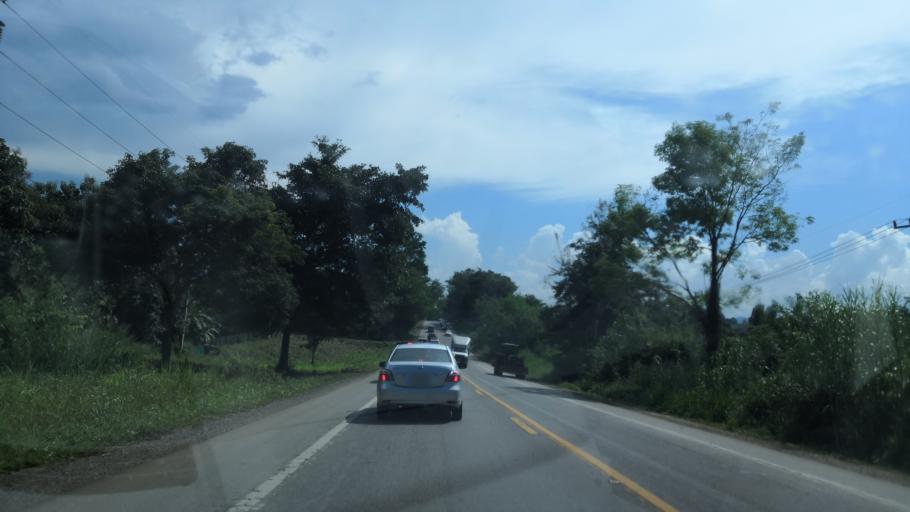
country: TH
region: Chiang Rai
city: Wiang Pa Pao
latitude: 19.4150
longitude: 99.5000
